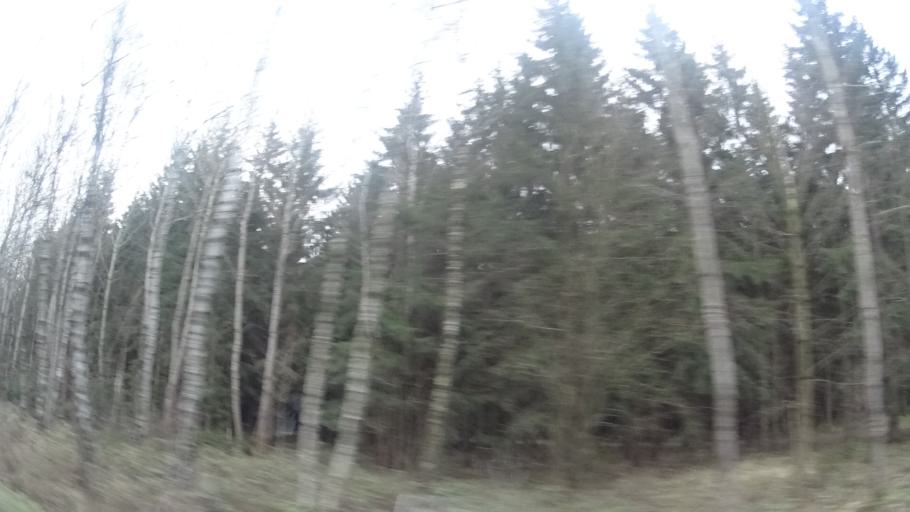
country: DE
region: Thuringia
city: Zeulenroda
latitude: 50.6261
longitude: 11.9989
